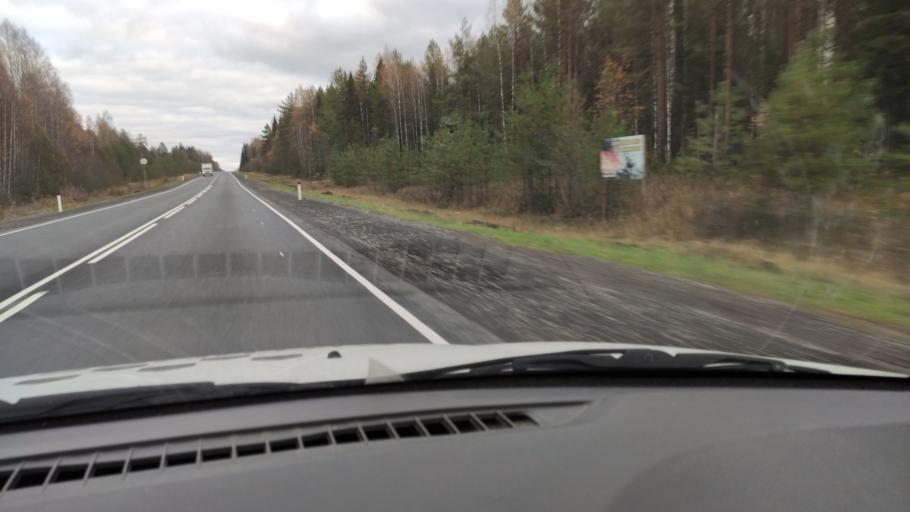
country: RU
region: Kirov
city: Chernaya Kholunitsa
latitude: 58.8880
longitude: 51.3750
